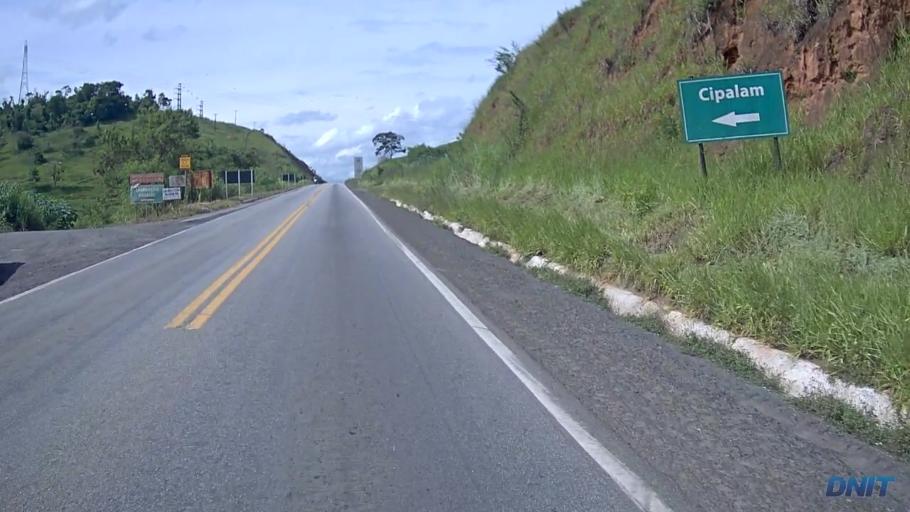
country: BR
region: Minas Gerais
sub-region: Ipatinga
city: Ipatinga
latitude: -19.4186
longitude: -42.4934
